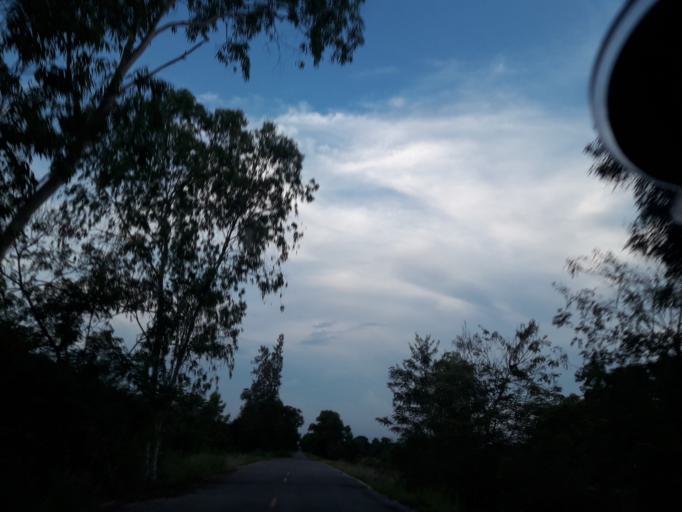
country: TH
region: Pathum Thani
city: Nong Suea
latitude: 14.2270
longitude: 100.8688
